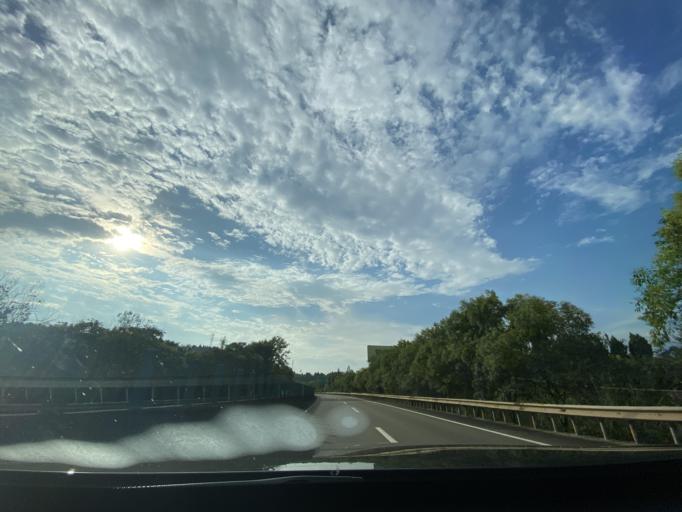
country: CN
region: Sichuan
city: Jiancheng
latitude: 30.2723
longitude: 104.6025
